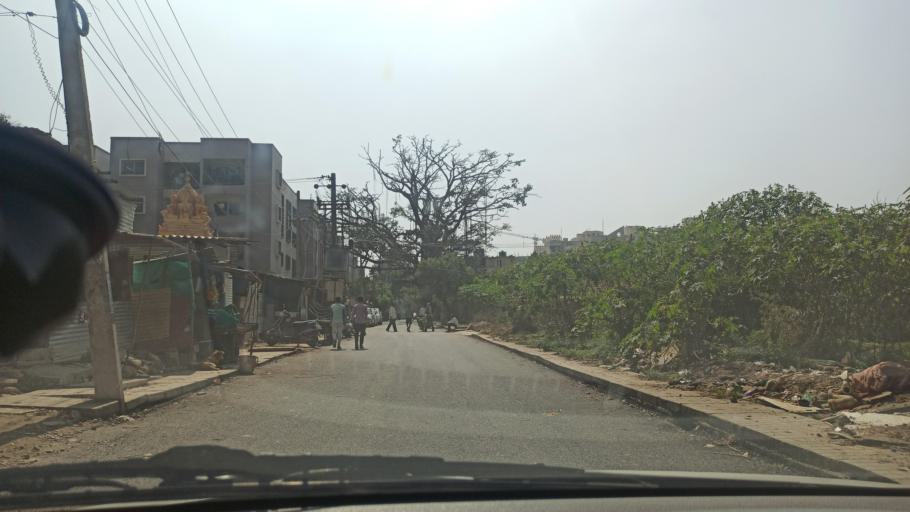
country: IN
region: Karnataka
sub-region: Bangalore Urban
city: Bangalore
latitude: 12.9356
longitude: 77.6864
